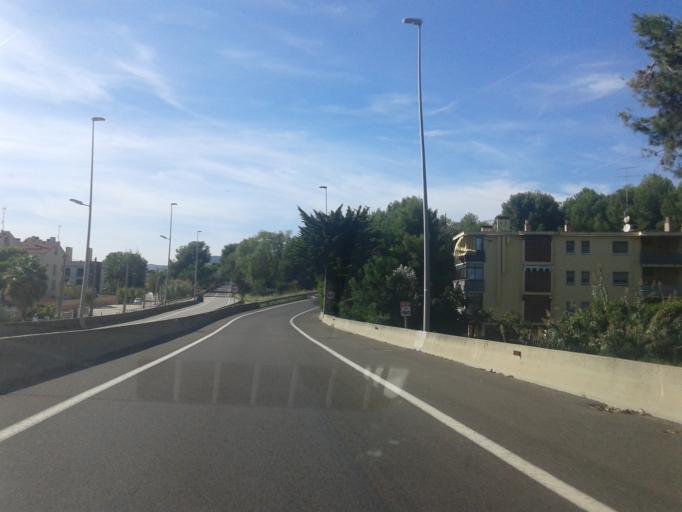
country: ES
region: Catalonia
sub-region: Provincia de Barcelona
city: Castelldefels
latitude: 41.2685
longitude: 1.9692
